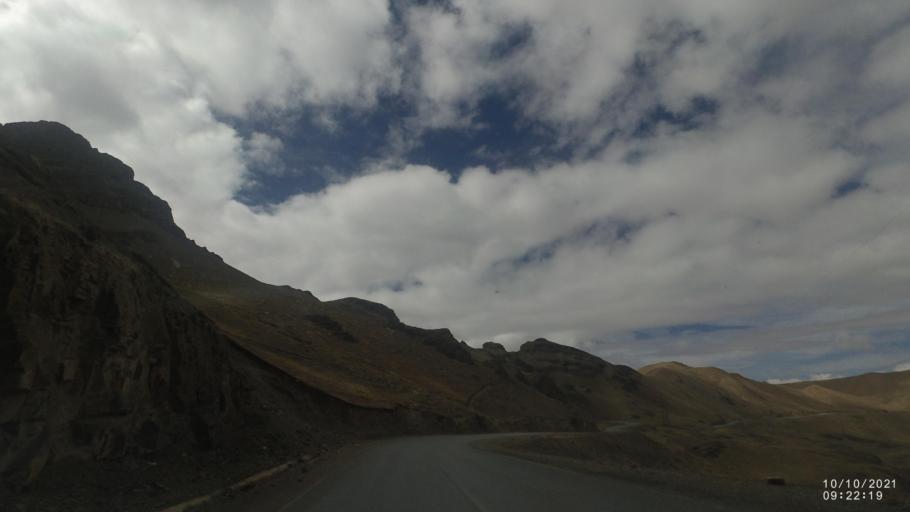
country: BO
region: La Paz
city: Quime
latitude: -17.0758
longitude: -67.2990
